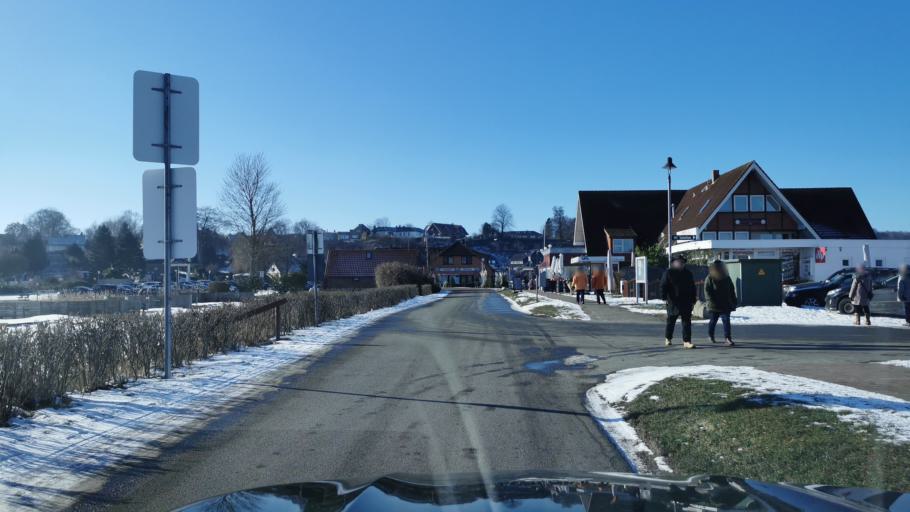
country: DE
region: Schleswig-Holstein
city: Westerholz
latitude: 54.8216
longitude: 9.6558
